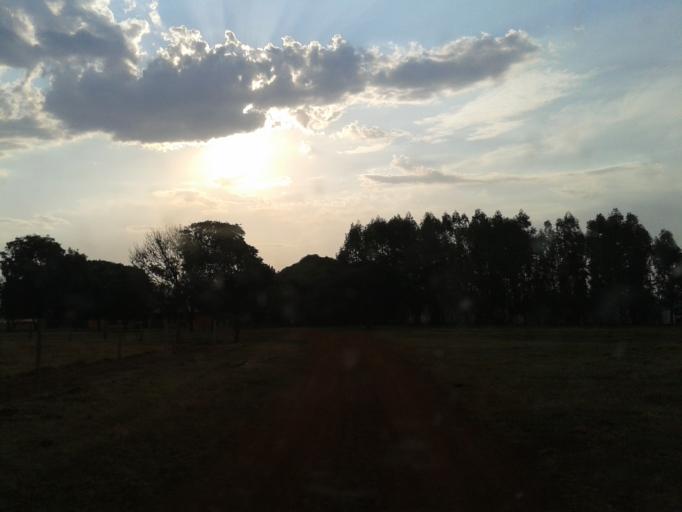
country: BR
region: Minas Gerais
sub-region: Capinopolis
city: Capinopolis
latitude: -18.7648
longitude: -49.7237
